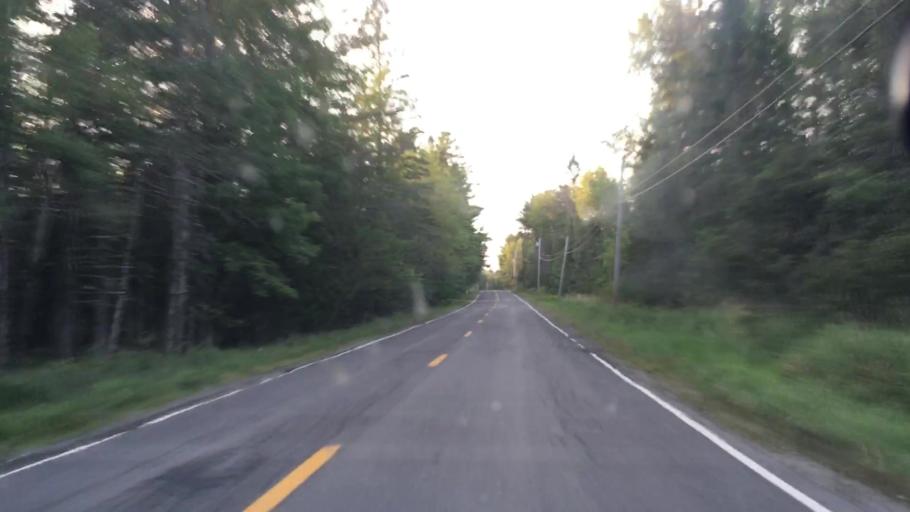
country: US
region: Maine
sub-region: Penobscot County
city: Hermon
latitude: 44.7052
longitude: -68.9481
